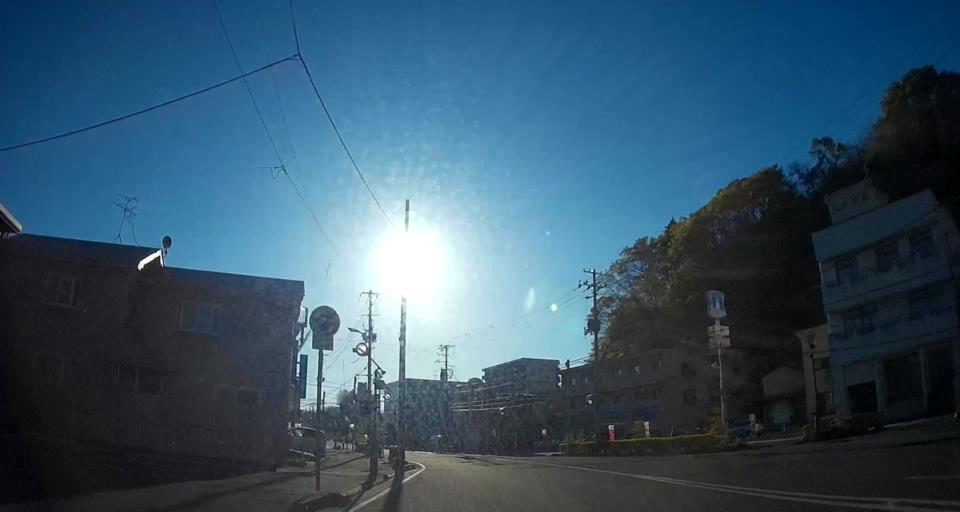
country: JP
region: Iwate
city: Miyako
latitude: 39.6423
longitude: 141.9564
